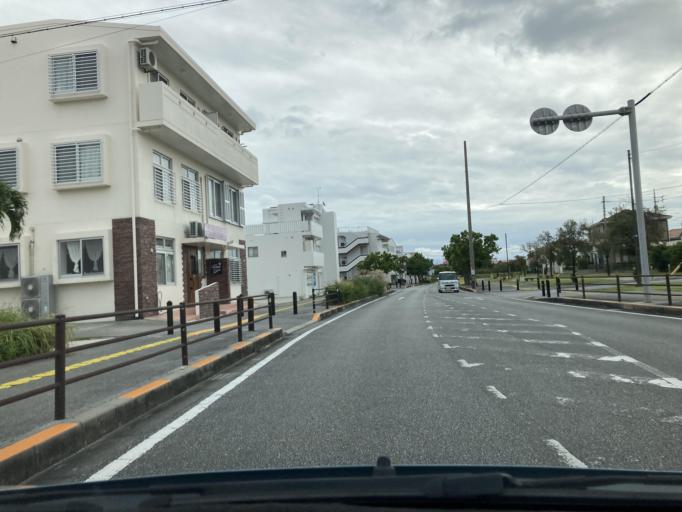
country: JP
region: Okinawa
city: Itoman
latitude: 26.1548
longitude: 127.6623
